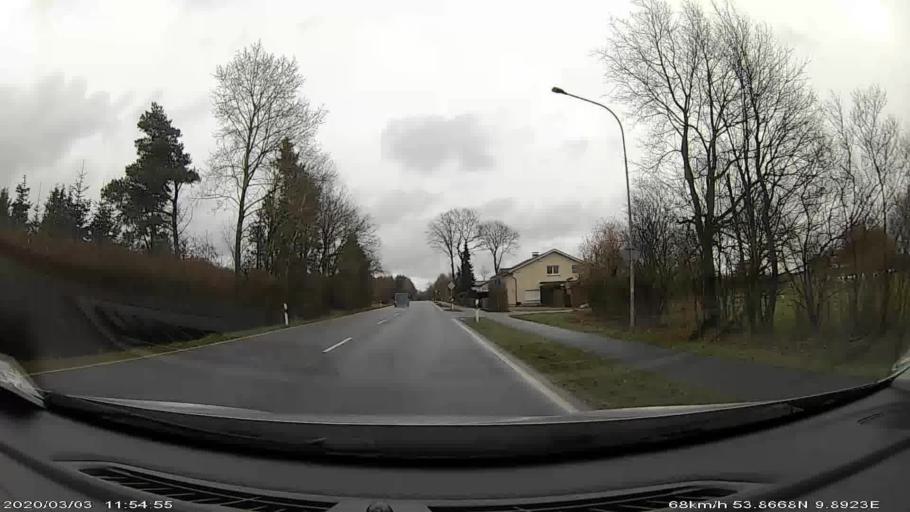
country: DE
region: Schleswig-Holstein
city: Lentfohrden
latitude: 53.8665
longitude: 9.8964
